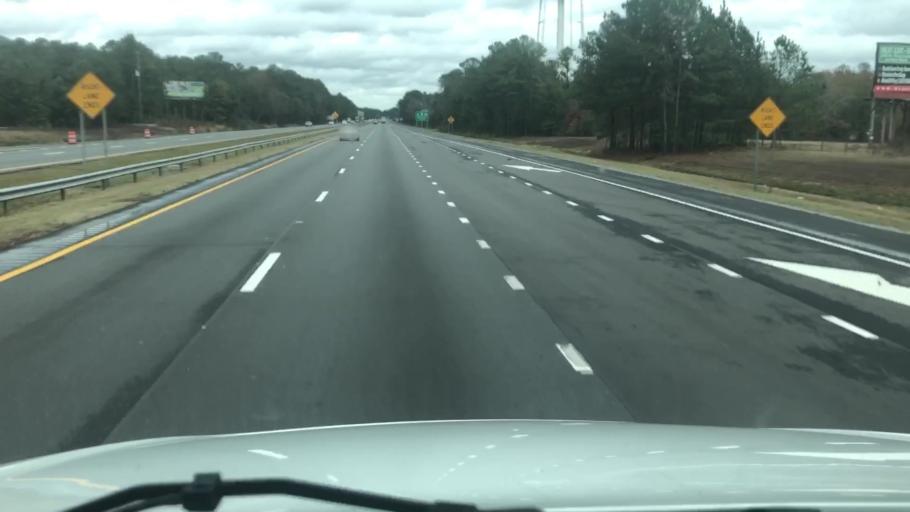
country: US
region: North Carolina
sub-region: Cumberland County
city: Eastover
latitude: 35.0974
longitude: -78.7761
